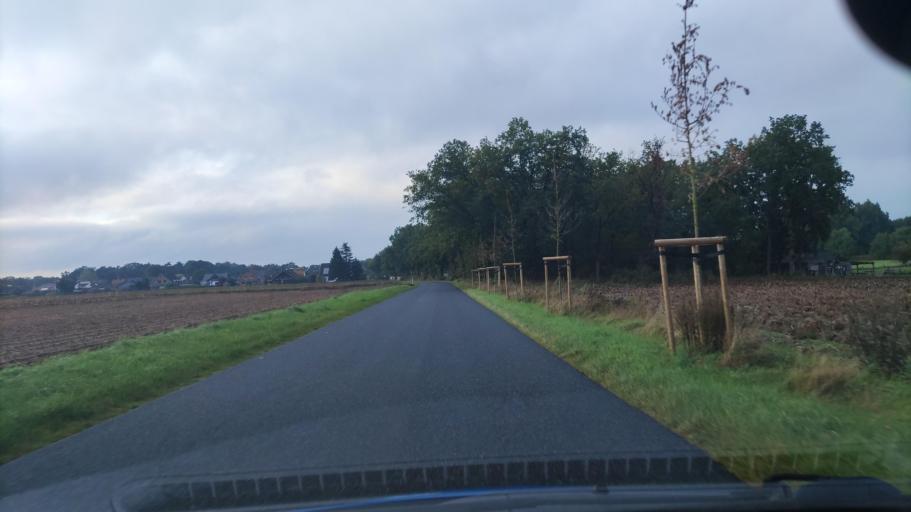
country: DE
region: Lower Saxony
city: Wrestedt
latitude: 52.9048
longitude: 10.6071
